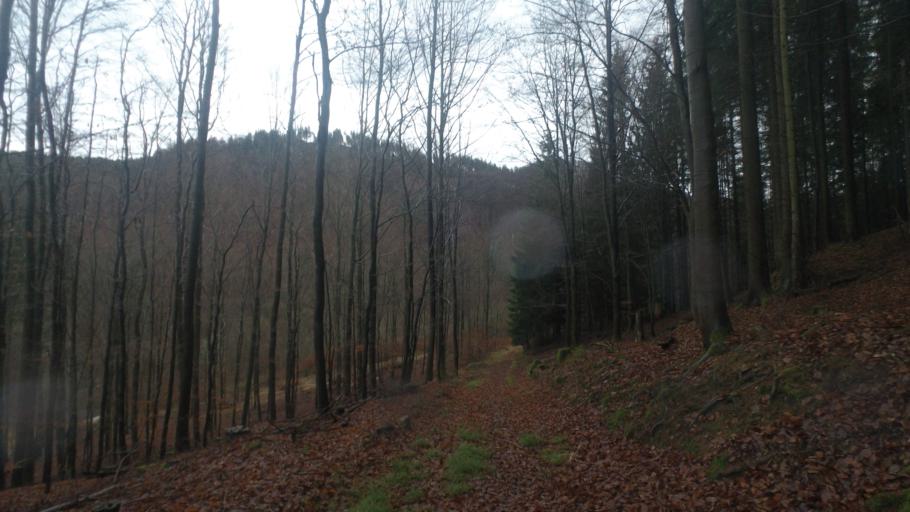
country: DE
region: Thuringia
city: Grafenroda
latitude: 50.7235
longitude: 10.7927
